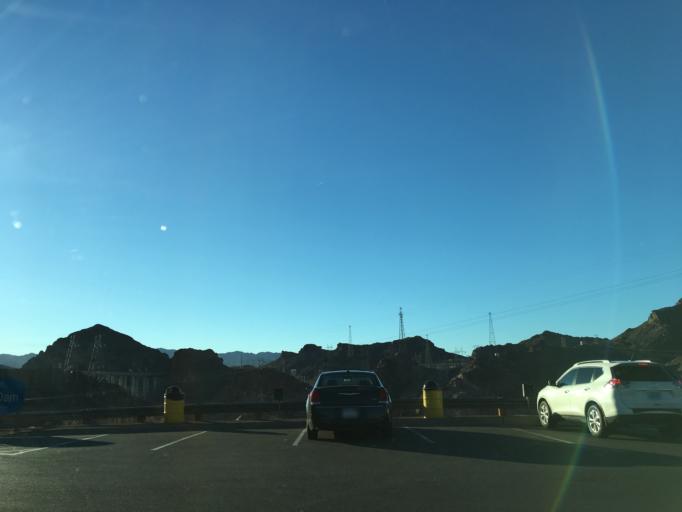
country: US
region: Nevada
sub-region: Clark County
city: Boulder City
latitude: 36.0136
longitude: -114.7319
